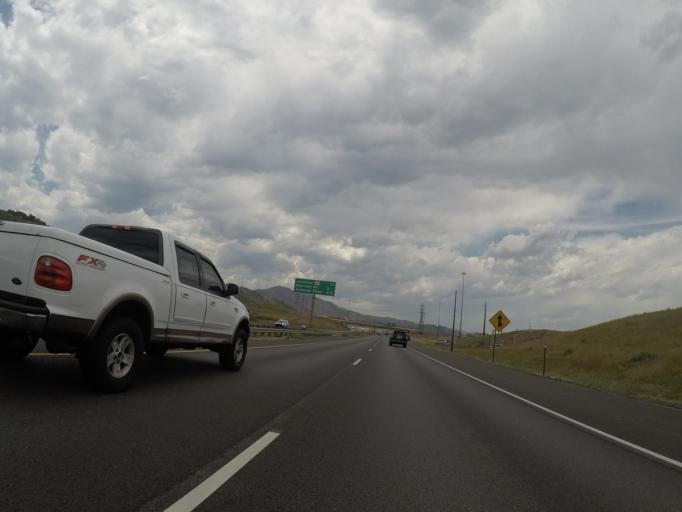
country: US
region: Colorado
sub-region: Jefferson County
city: Ken Caryl
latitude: 39.6287
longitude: -105.1571
